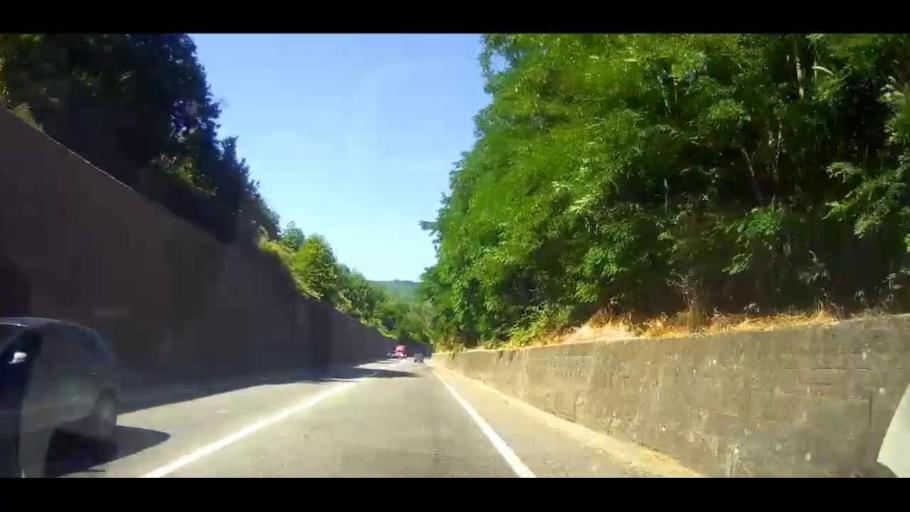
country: IT
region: Calabria
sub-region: Provincia di Cosenza
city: Celico
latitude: 39.3119
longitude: 16.3284
